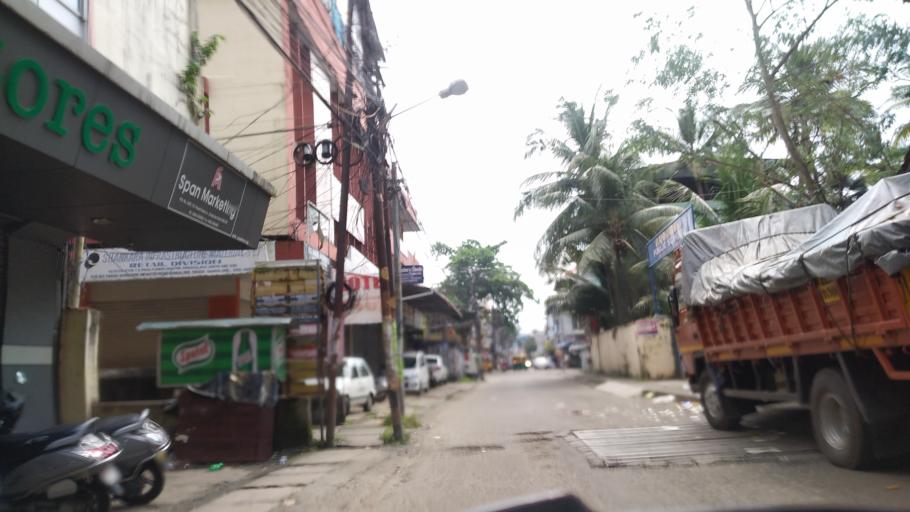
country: IN
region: Kerala
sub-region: Ernakulam
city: Cochin
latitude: 9.9818
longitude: 76.2809
